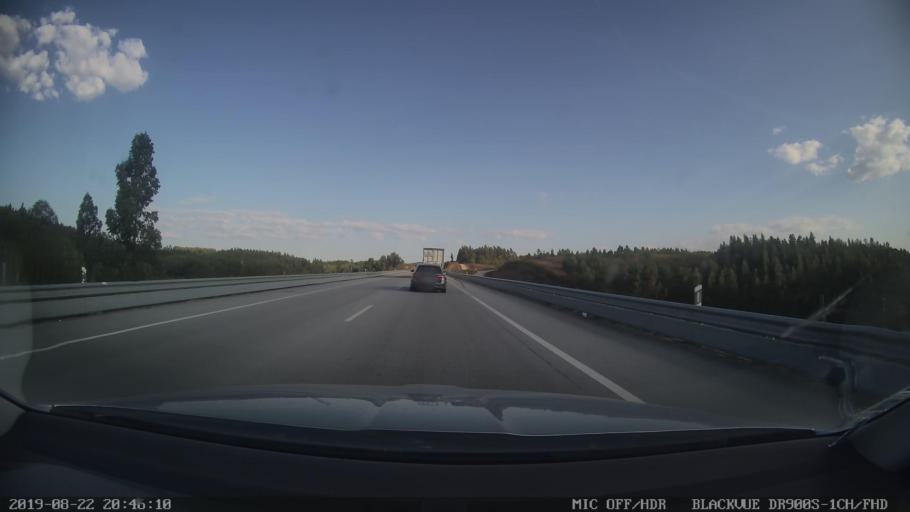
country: PT
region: Castelo Branco
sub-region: Proenca-A-Nova
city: Proenca-a-Nova
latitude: 39.7240
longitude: -7.8738
